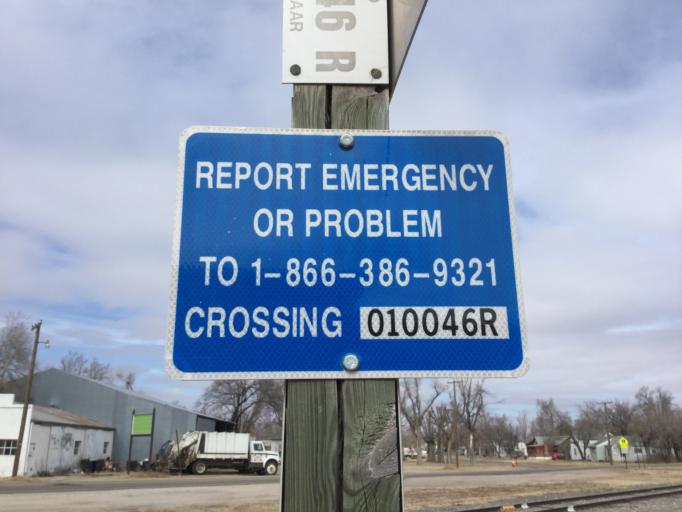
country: US
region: Kansas
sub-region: Pawnee County
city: Larned
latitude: 38.1797
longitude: -99.0947
